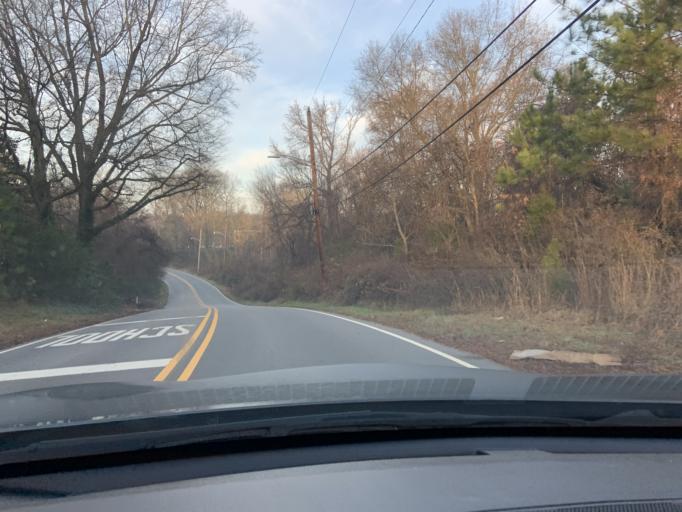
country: US
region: North Carolina
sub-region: Mecklenburg County
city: Charlotte
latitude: 35.2314
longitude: -80.9132
